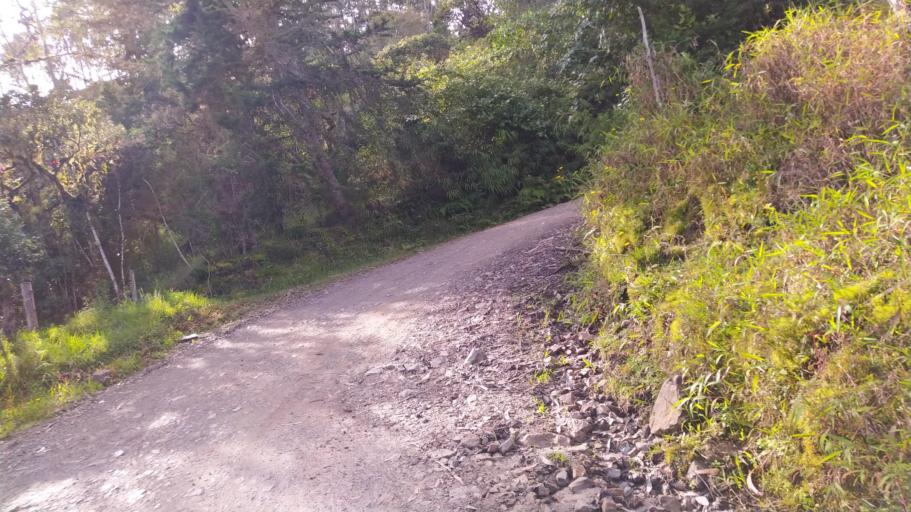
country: CO
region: Cundinamarca
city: Tenza
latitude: 5.0896
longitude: -73.4755
